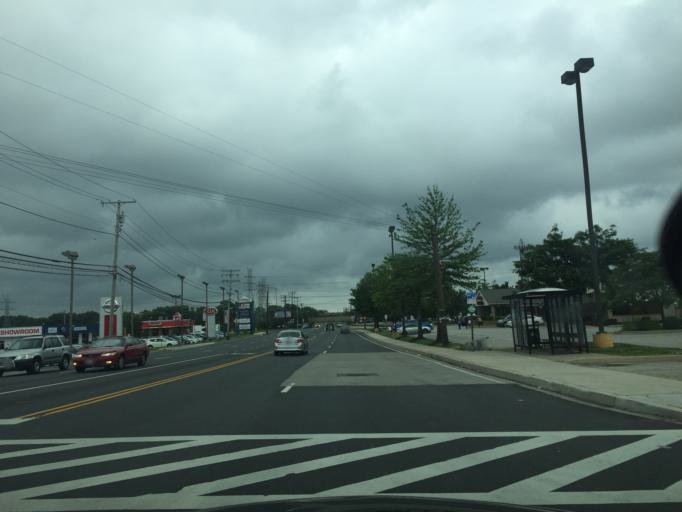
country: US
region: Maryland
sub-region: Baltimore County
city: Rosedale
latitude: 39.2956
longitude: -76.5095
